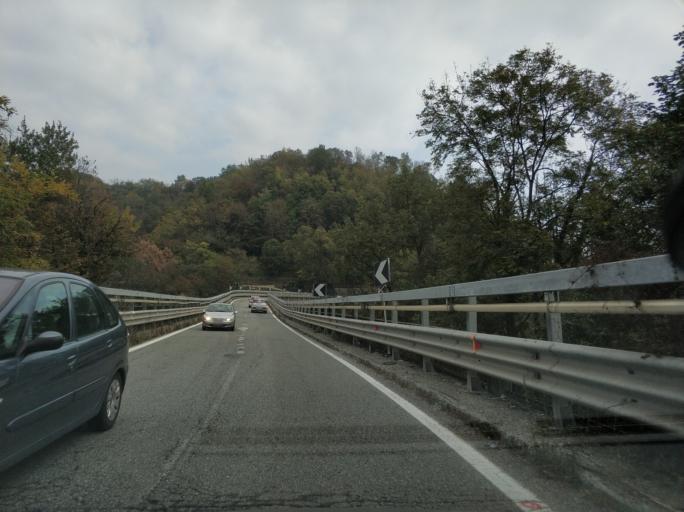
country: IT
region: Piedmont
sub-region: Provincia di Torino
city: Baldissero Canavese
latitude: 45.4142
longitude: 7.7542
